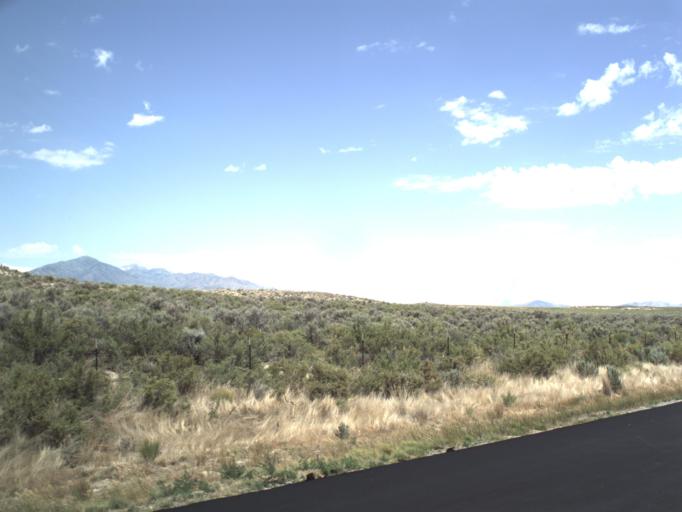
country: US
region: Utah
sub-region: Tooele County
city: Tooele
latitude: 40.1938
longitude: -112.4153
